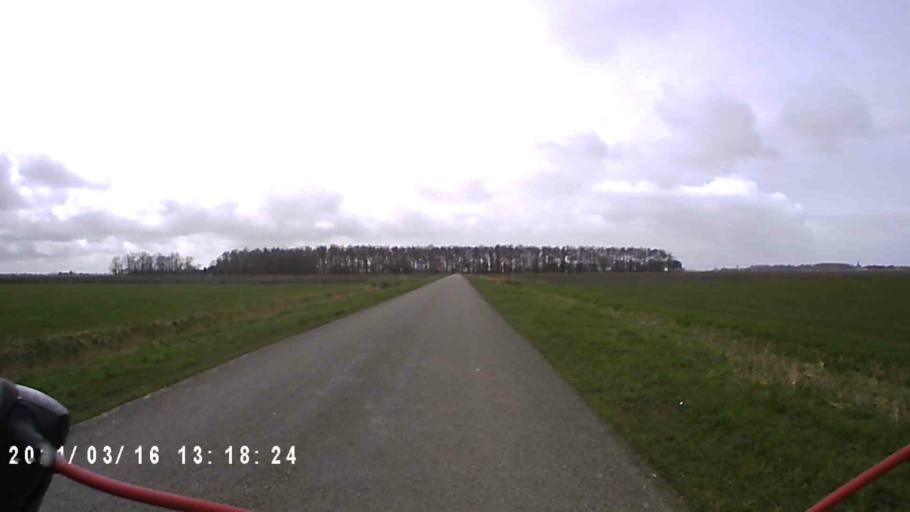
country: NL
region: Friesland
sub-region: Gemeente Het Bildt
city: Minnertsga
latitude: 53.2358
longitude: 5.5848
